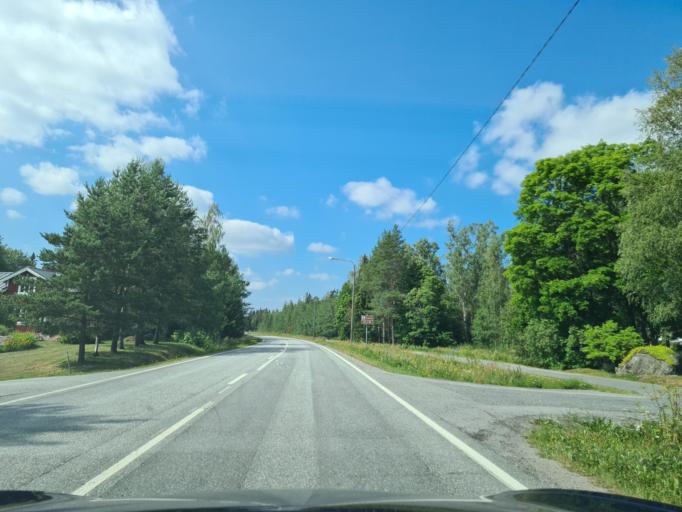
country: FI
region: Ostrobothnia
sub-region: Vaasa
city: Vaasa
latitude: 63.1942
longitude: 21.5543
